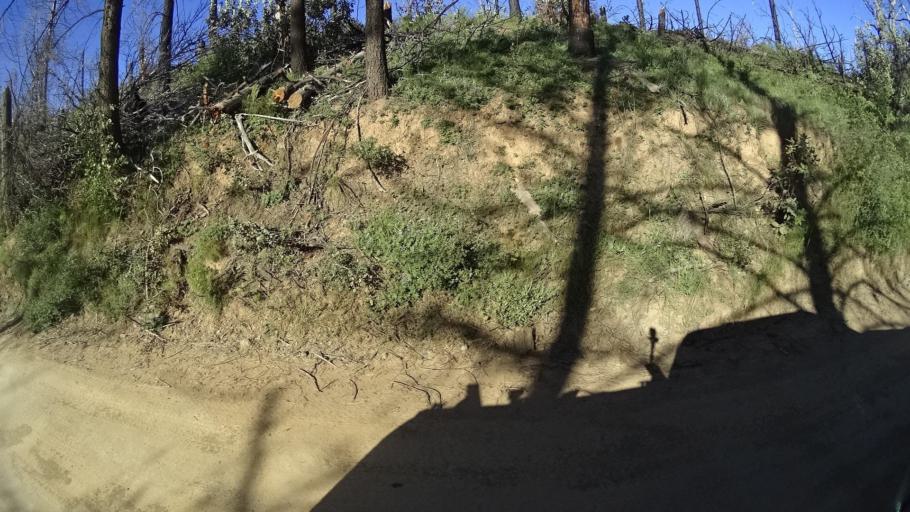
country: US
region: California
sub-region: Lake County
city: Upper Lake
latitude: 39.3435
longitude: -122.9615
